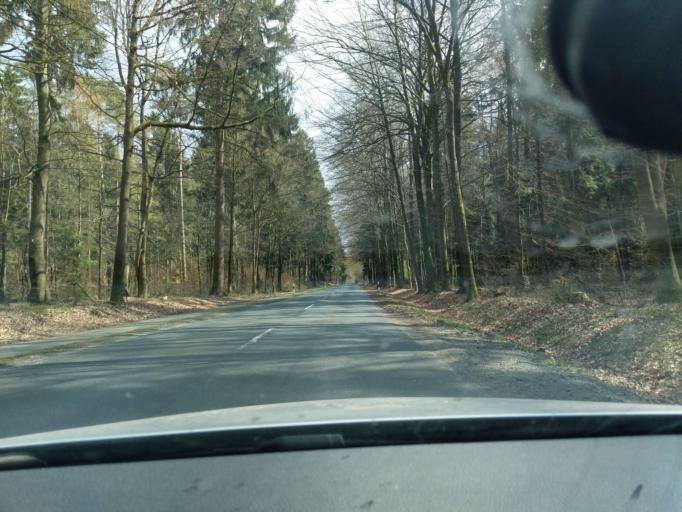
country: DE
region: Lower Saxony
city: Dollern
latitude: 53.5180
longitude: 9.5163
